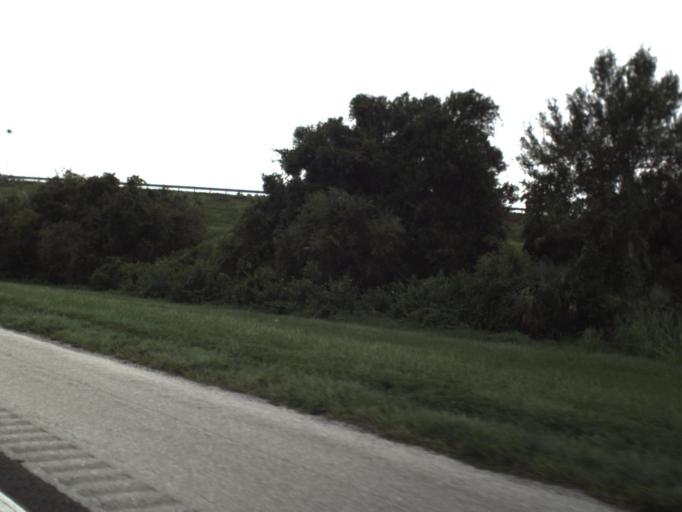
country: US
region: Florida
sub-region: Manatee County
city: Ellenton
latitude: 27.5853
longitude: -82.5146
